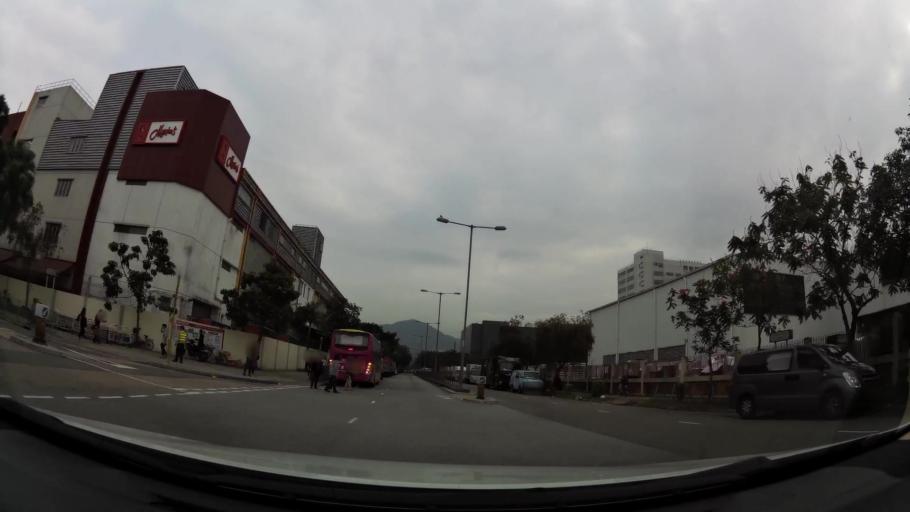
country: HK
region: Tai Po
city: Tai Po
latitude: 22.4593
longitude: 114.1883
